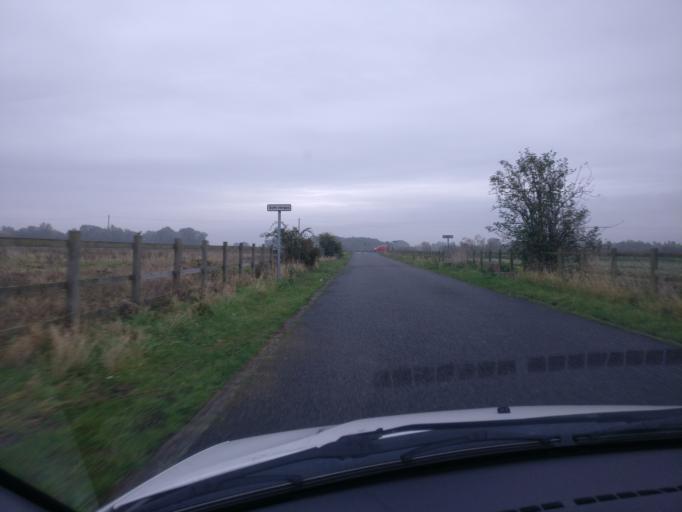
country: GB
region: England
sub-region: Peterborough
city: Eye
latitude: 52.5754
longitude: -0.1864
